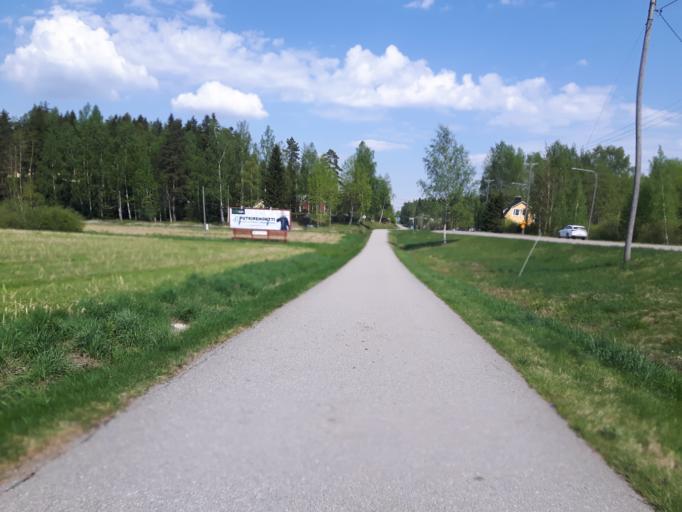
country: FI
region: Uusimaa
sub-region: Porvoo
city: Porvoo
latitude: 60.3824
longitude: 25.6209
